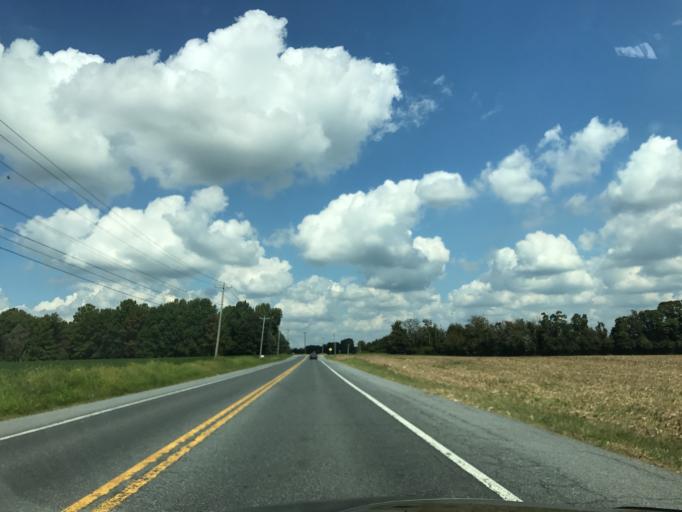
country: US
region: Maryland
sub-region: Queen Anne's County
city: Centreville
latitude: 39.0261
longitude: -76.0773
